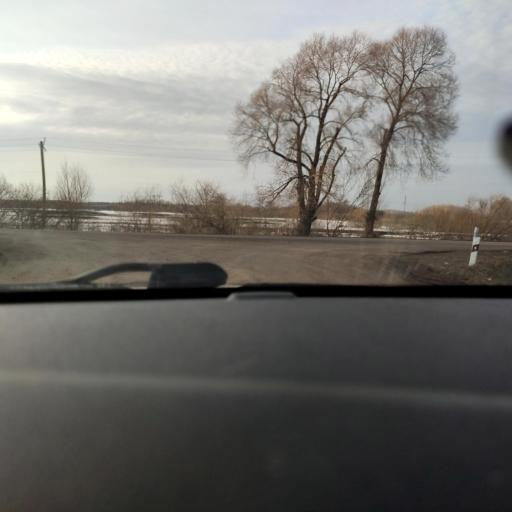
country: RU
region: Bashkortostan
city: Avdon
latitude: 54.4873
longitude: 55.5902
